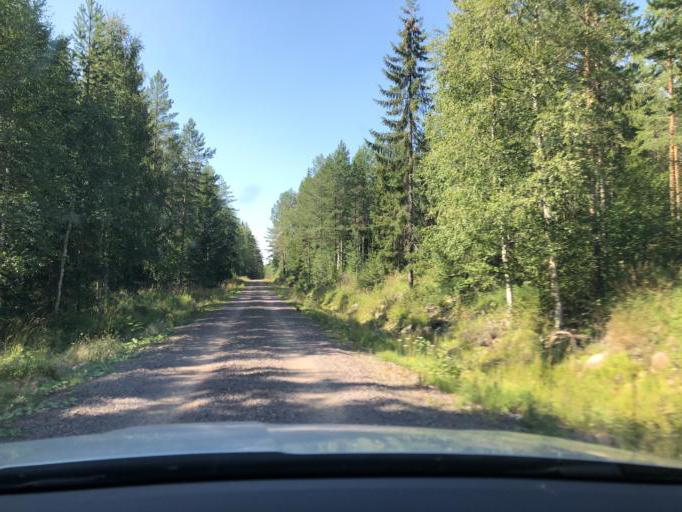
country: SE
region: Dalarna
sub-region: Orsa Kommun
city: Orsa
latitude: 61.2201
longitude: 14.7242
